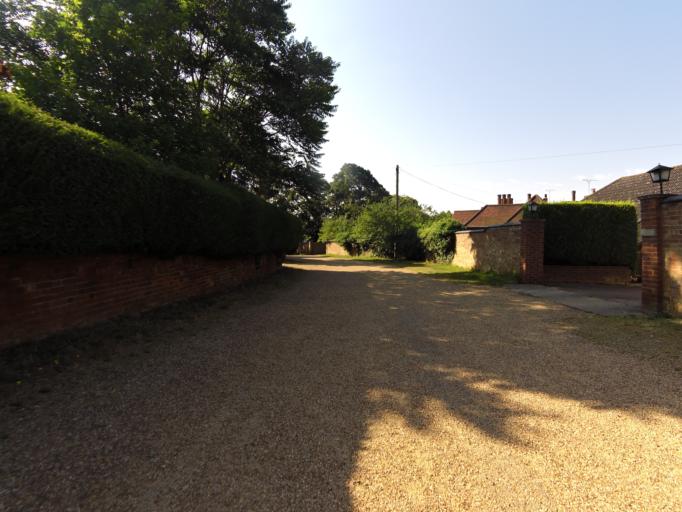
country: GB
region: England
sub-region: Suffolk
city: Ipswich
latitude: 52.0675
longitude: 1.1522
